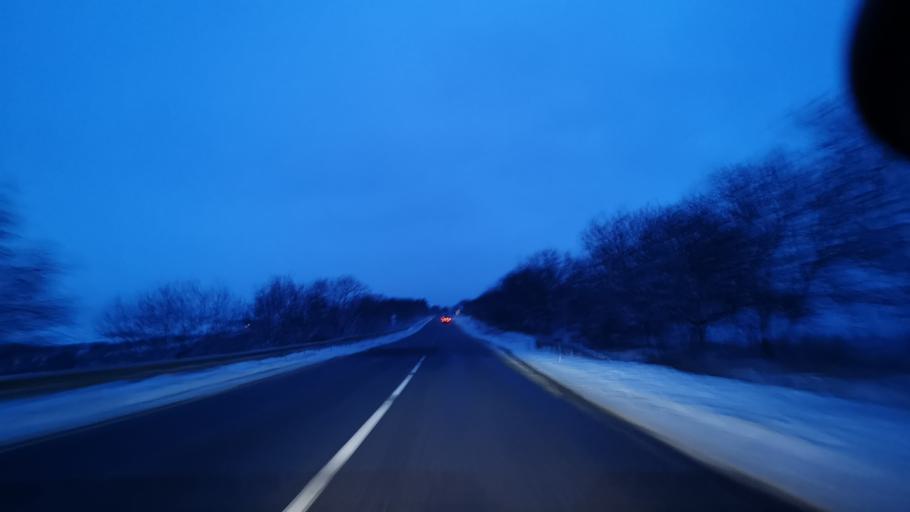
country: MD
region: Orhei
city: Orhei
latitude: 47.5719
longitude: 28.7980
